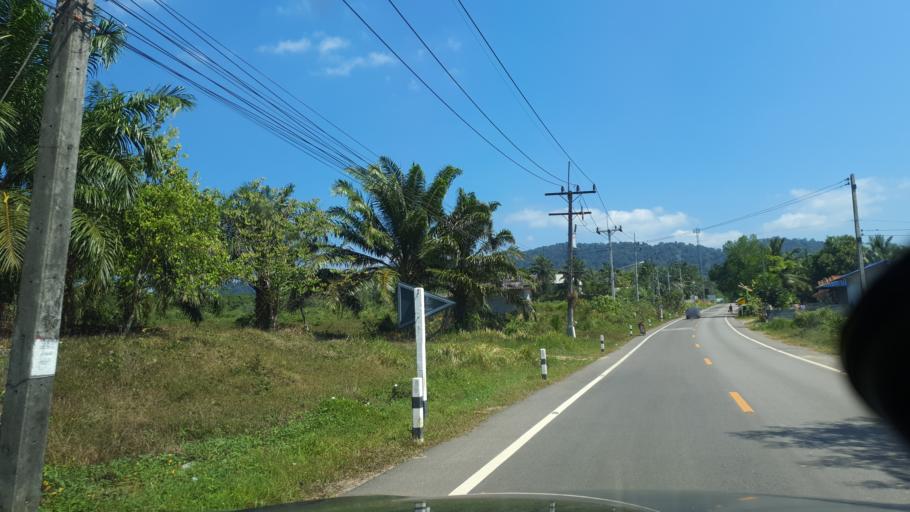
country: TH
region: Krabi
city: Khlong Thom
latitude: 7.9209
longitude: 99.2569
